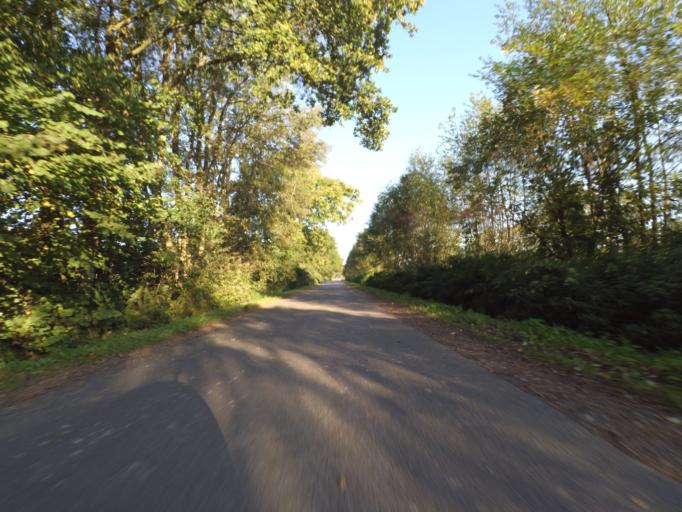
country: NL
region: Gelderland
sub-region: Gemeente Barneveld
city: Terschuur
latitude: 52.1736
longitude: 5.5321
